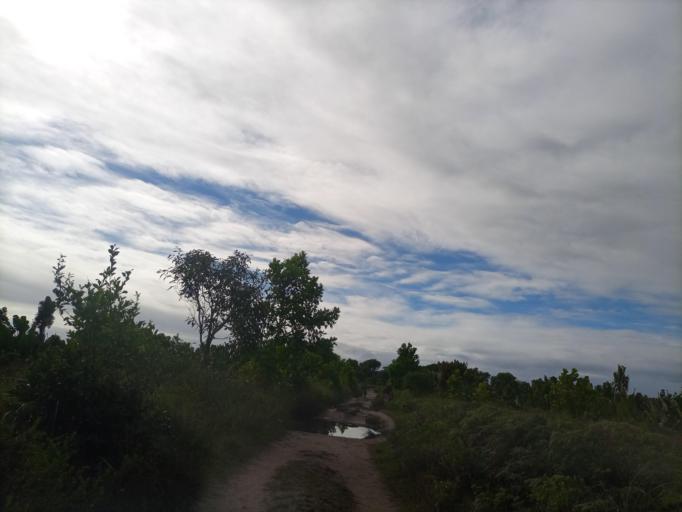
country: MG
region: Anosy
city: Fort Dauphin
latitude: -24.7793
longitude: 47.1858
